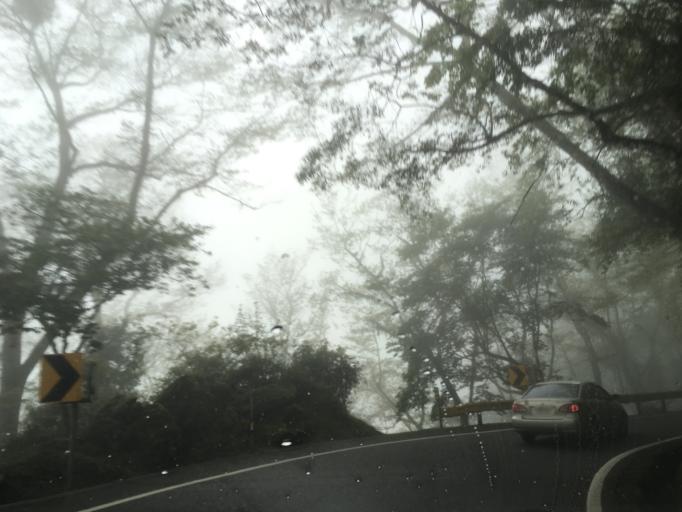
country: TW
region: Taiwan
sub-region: Hualien
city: Hualian
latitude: 24.1854
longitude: 121.4172
